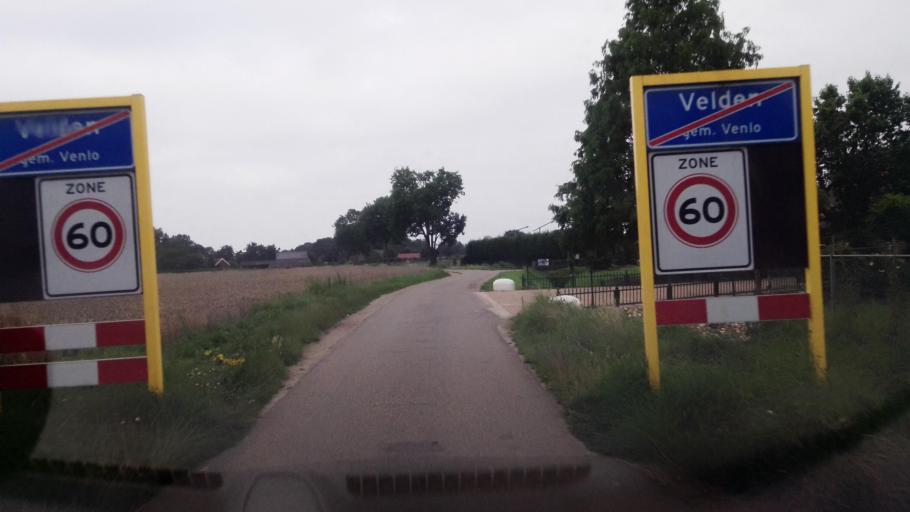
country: NL
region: Limburg
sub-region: Gemeente Venlo
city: Venlo
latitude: 51.4160
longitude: 6.1606
